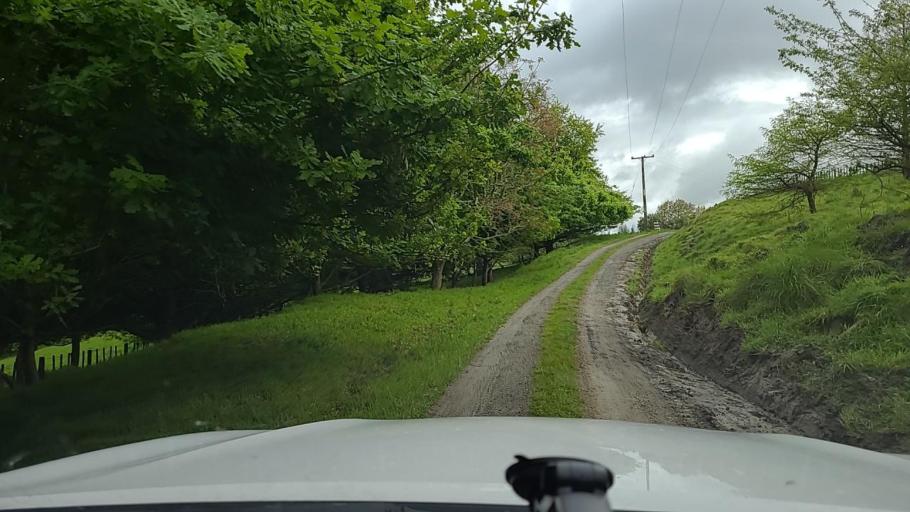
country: NZ
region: Gisborne
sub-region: Gisborne District
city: Gisborne
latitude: -38.4408
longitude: 177.6991
